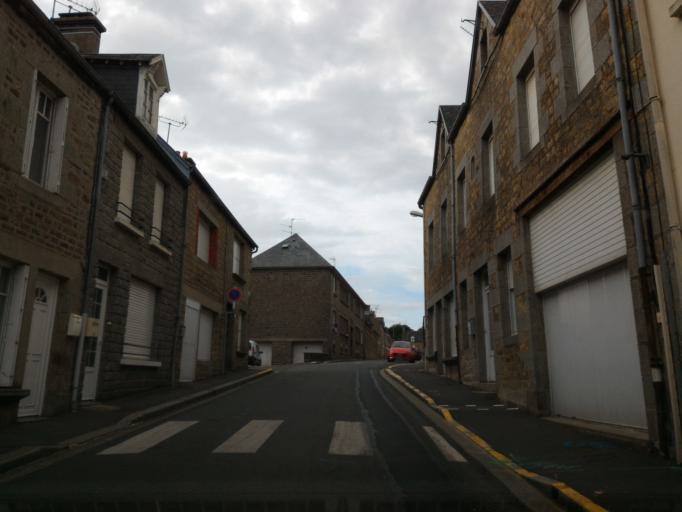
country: FR
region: Lower Normandy
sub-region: Departement de la Manche
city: La Haye-Pesnel
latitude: 48.7955
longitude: -1.3962
